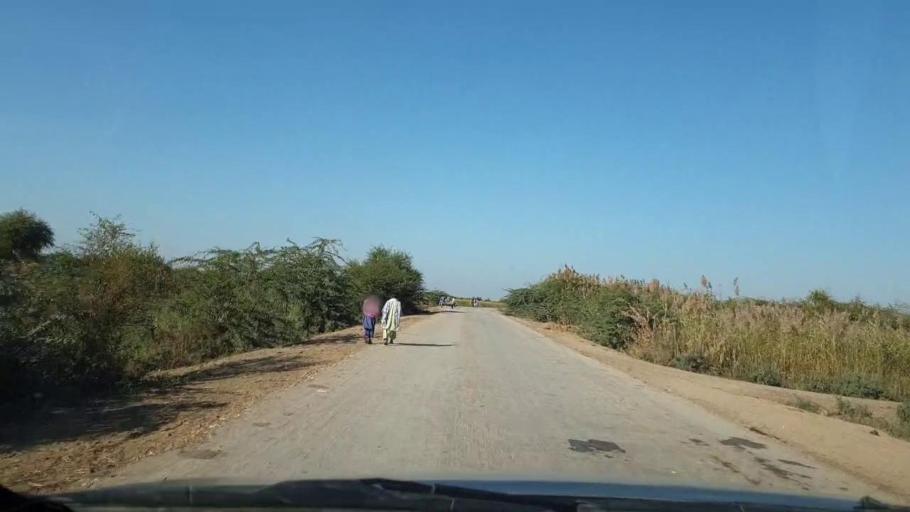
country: PK
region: Sindh
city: Berani
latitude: 25.8184
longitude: 68.9479
